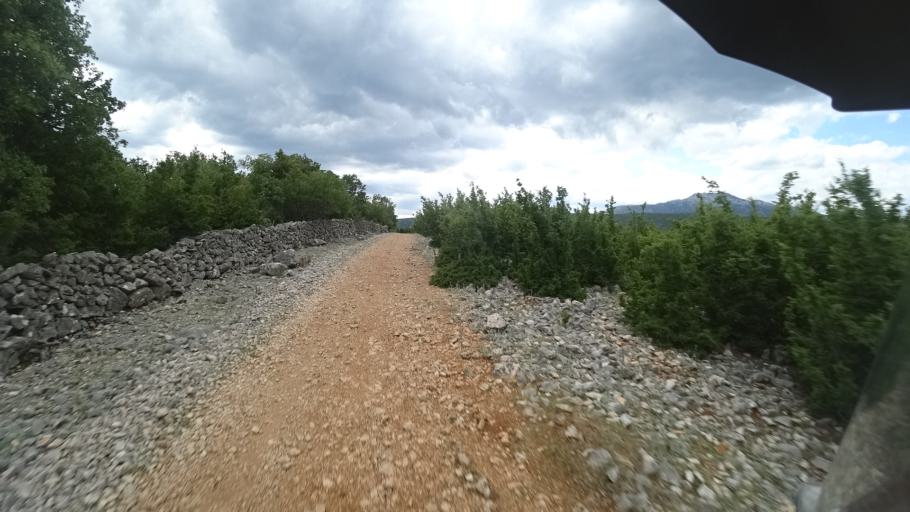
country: HR
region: Zadarska
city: Gracac
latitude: 44.1871
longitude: 15.8978
